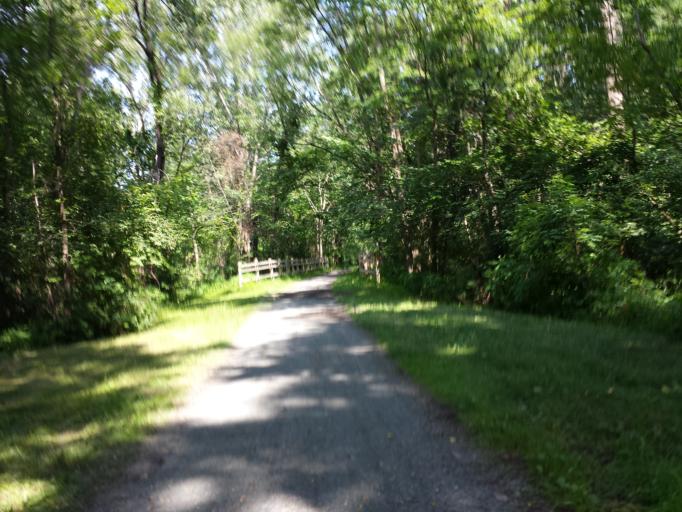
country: US
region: New York
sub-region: Saratoga County
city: Country Knolls
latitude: 42.9174
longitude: -73.7702
